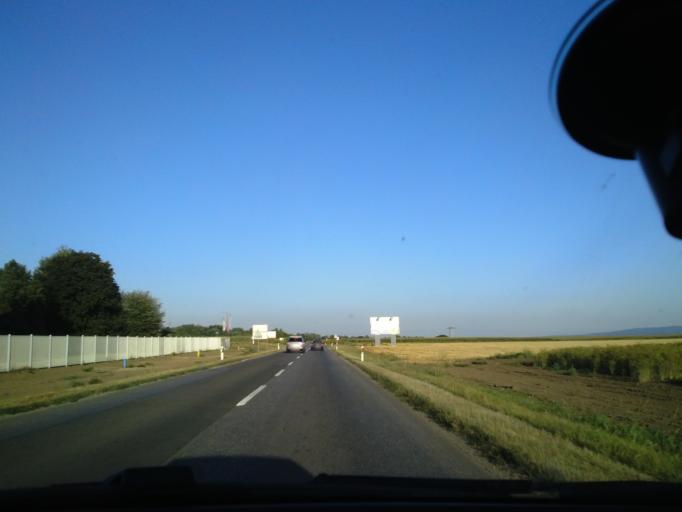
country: RS
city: Kisac
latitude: 45.3361
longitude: 19.6688
